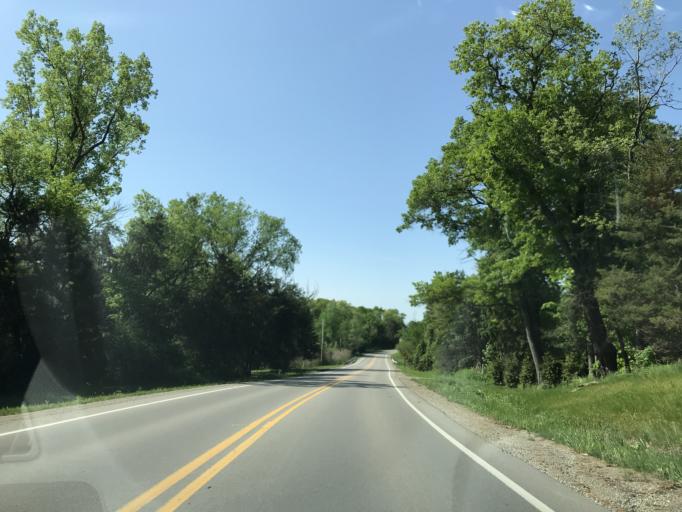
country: US
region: Michigan
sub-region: Oakland County
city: South Lyon
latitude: 42.4733
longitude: -83.6960
